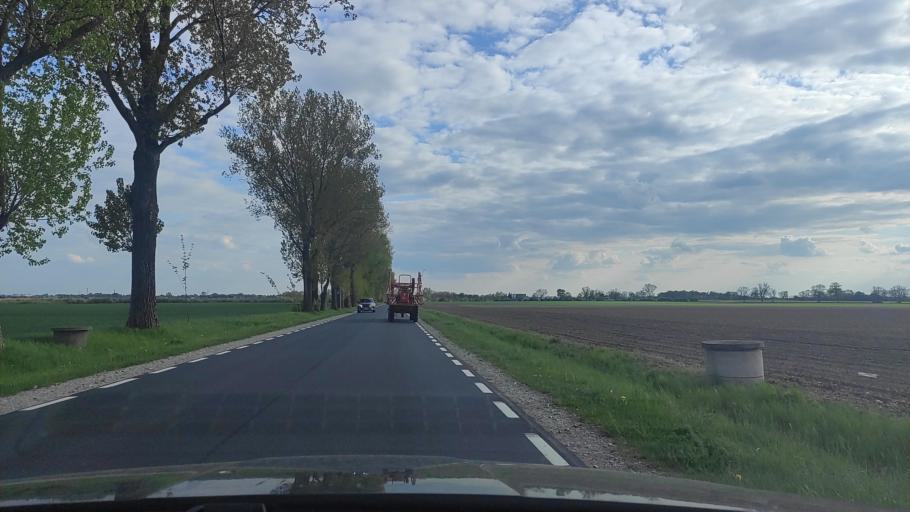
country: PL
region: Greater Poland Voivodeship
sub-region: Powiat poznanski
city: Kostrzyn
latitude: 52.4291
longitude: 17.2307
